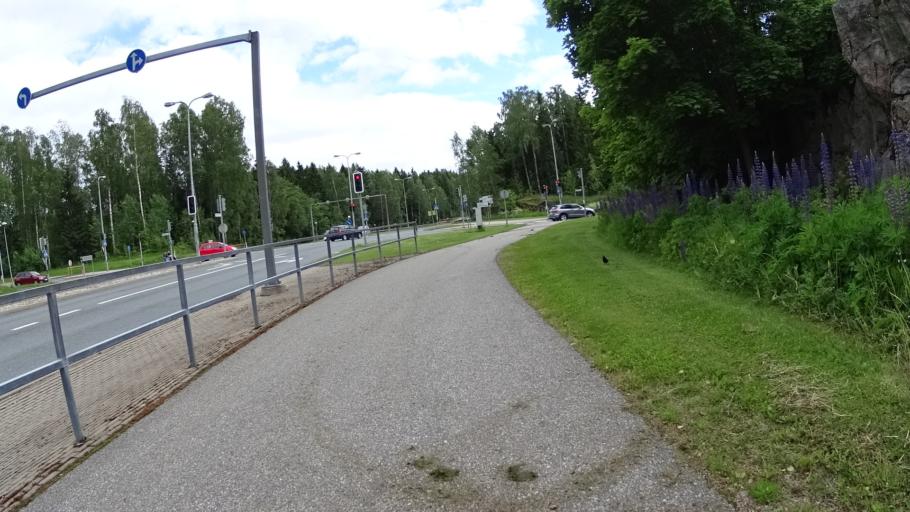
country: FI
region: Uusimaa
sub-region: Helsinki
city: Kilo
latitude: 60.2824
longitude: 24.8353
